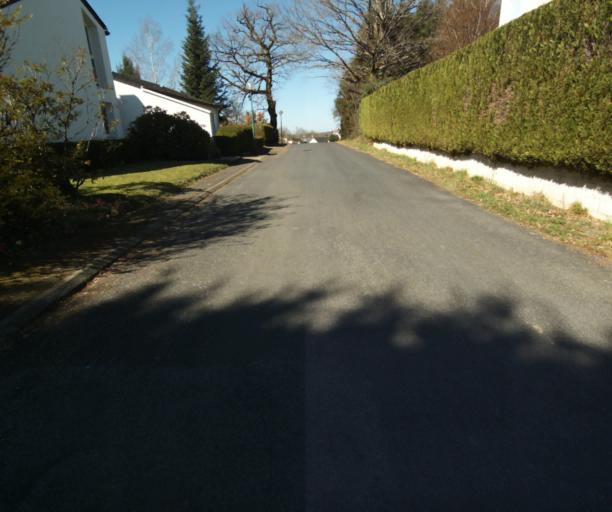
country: FR
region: Limousin
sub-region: Departement de la Correze
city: Chamboulive
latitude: 45.4267
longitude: 1.7054
